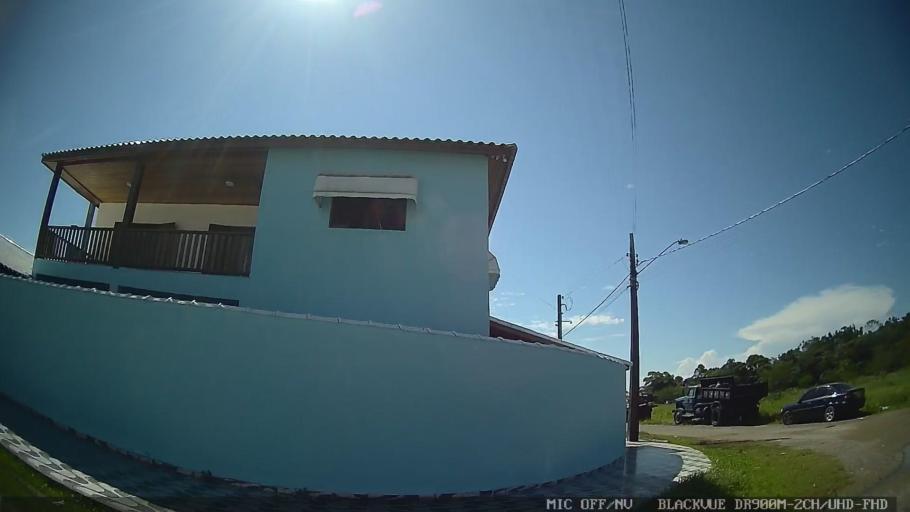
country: BR
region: Sao Paulo
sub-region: Iguape
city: Iguape
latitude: -24.6926
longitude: -47.5617
